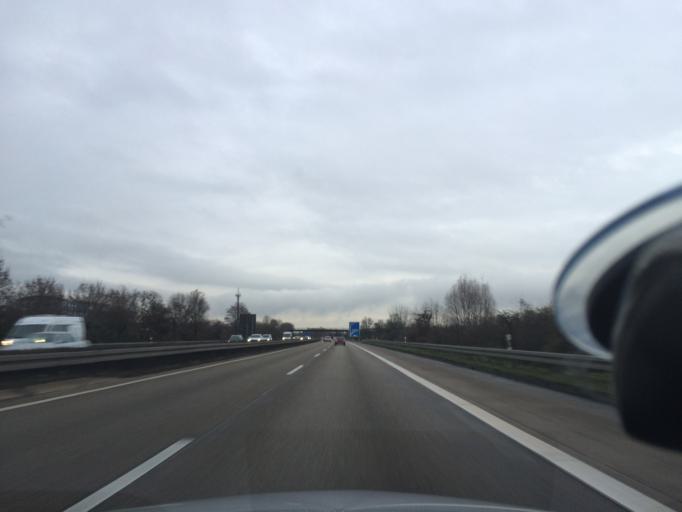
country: DE
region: Hesse
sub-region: Regierungsbezirk Darmstadt
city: Russelsheim
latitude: 49.9746
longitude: 8.4242
